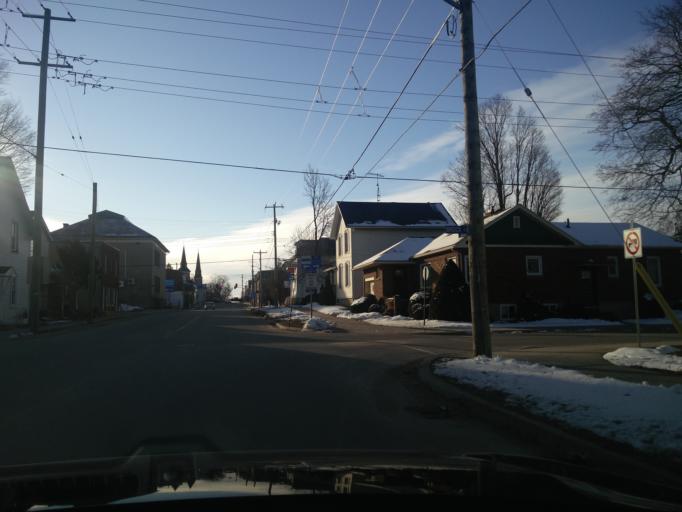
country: CA
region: Ontario
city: Gananoque
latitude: 44.3310
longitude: -76.1643
